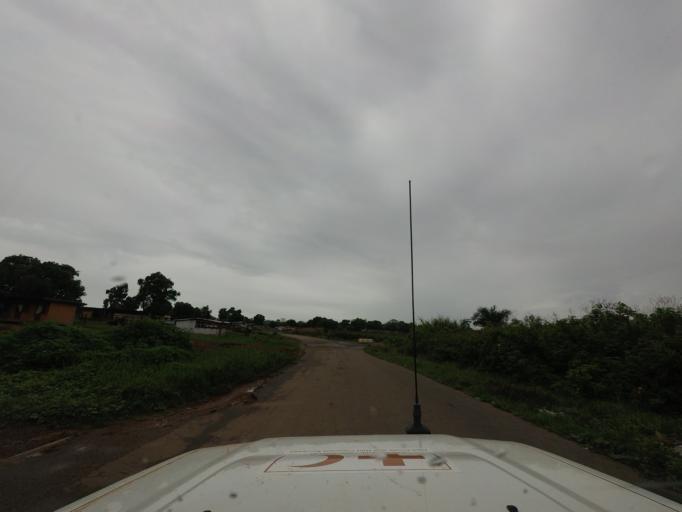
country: LR
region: Nimba
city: New Yekepa
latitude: 7.5692
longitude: -8.5463
